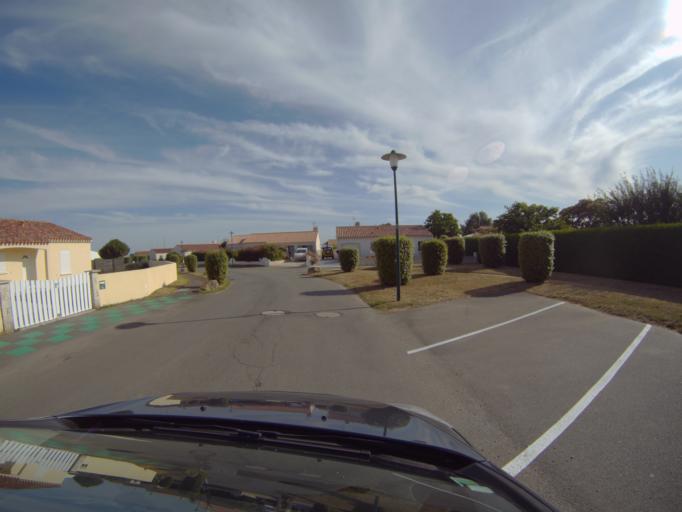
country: FR
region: Pays de la Loire
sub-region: Departement de la Vendee
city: Angles
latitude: 46.4097
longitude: -1.3955
